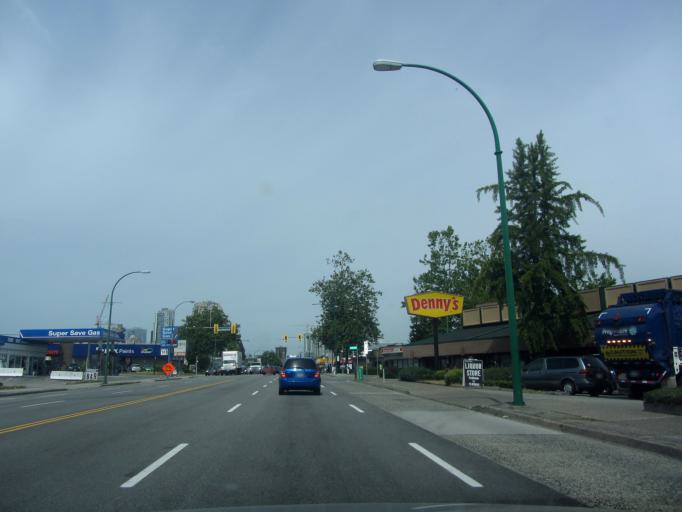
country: CA
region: British Columbia
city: Burnaby
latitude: 49.2185
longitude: -122.9597
